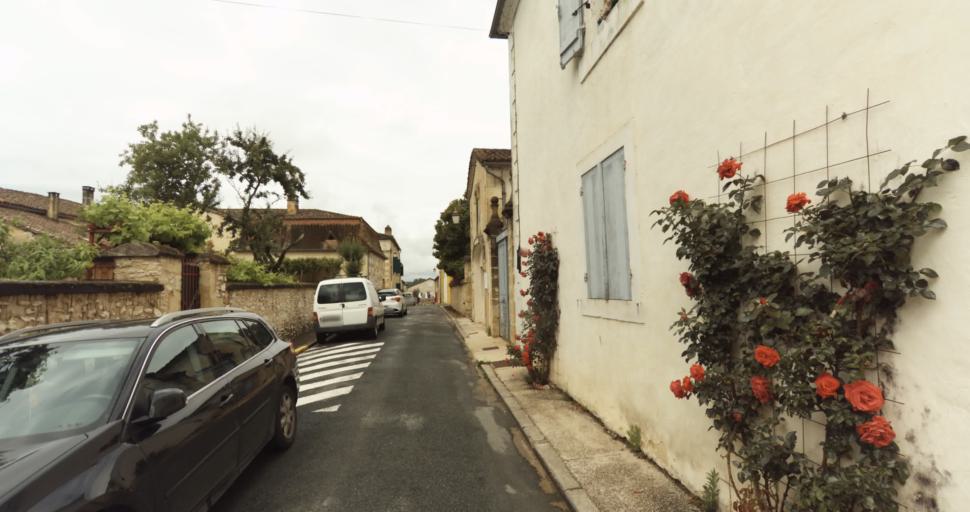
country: FR
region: Aquitaine
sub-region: Departement de la Dordogne
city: Belves
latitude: 44.6790
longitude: 0.8947
